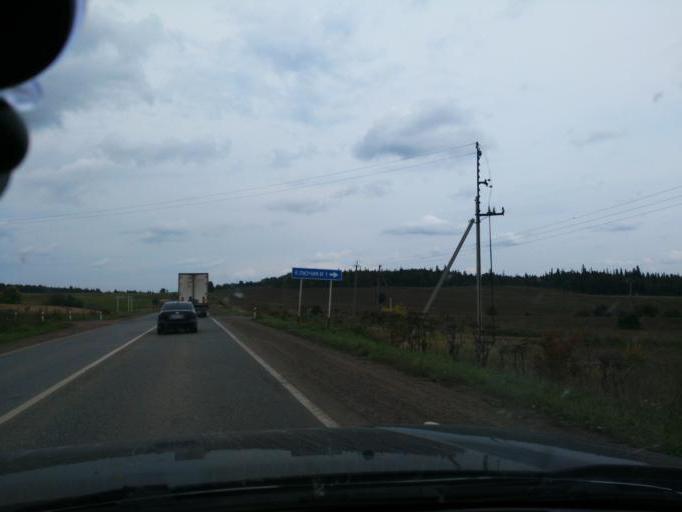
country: RU
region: Perm
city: Kuyeda
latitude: 56.4641
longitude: 55.6643
